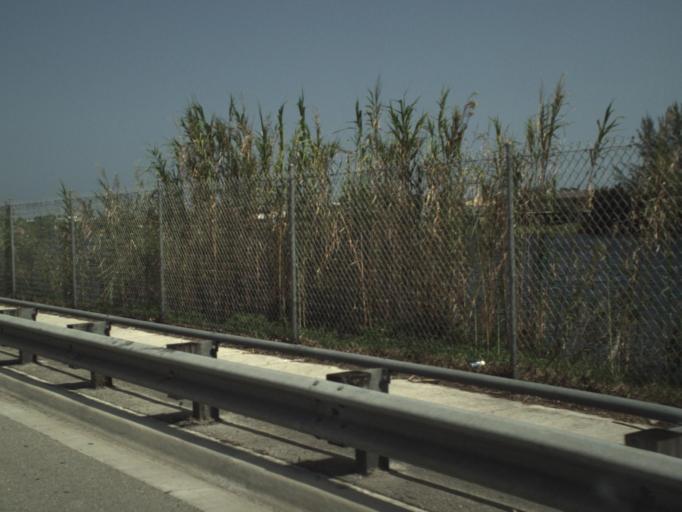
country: US
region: Florida
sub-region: Broward County
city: Tedder
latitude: 26.2747
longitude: -80.1418
